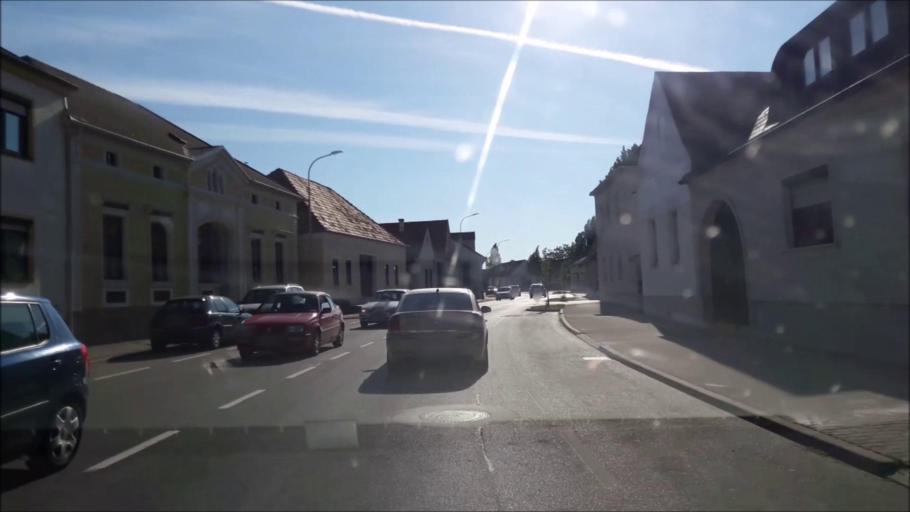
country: AT
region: Burgenland
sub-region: Eisenstadt-Umgebung
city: Trausdorf an der Wulka
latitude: 47.8140
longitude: 16.5574
